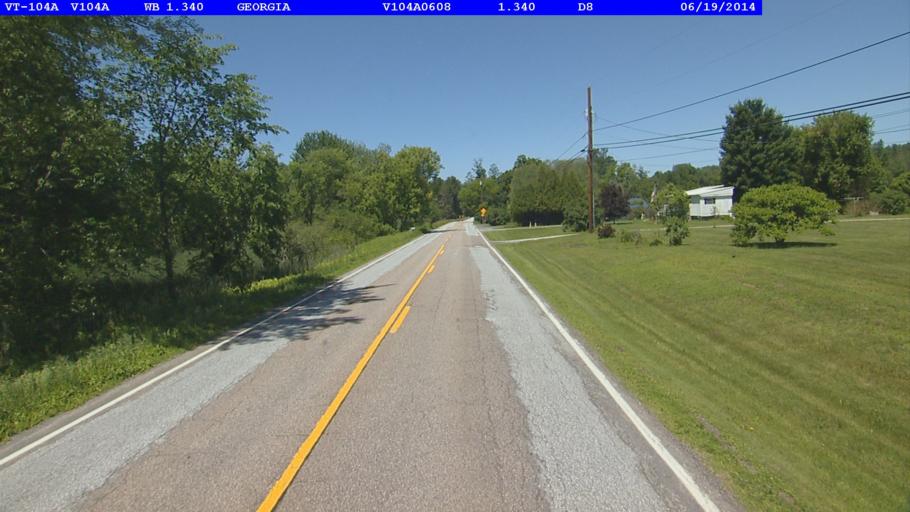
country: US
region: Vermont
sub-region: Chittenden County
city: Milton
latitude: 44.6827
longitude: -73.0887
